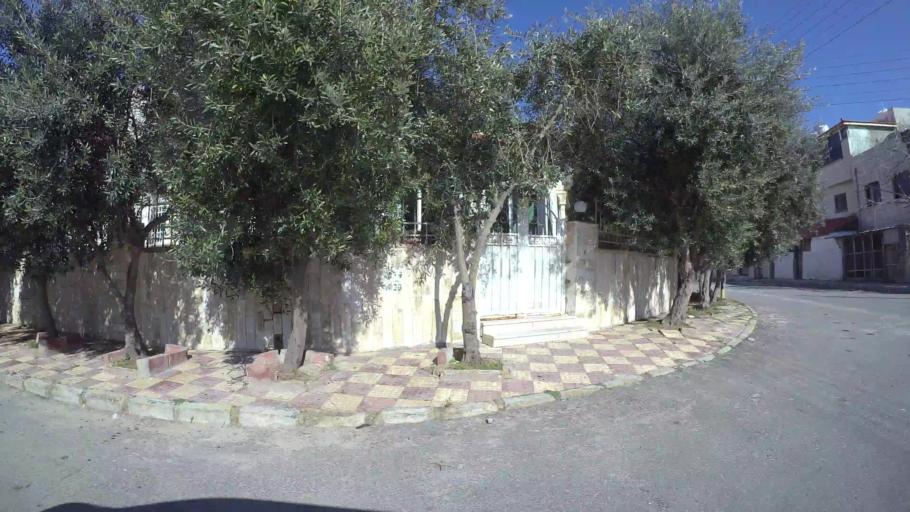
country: JO
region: Amman
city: Al Bunayyat ash Shamaliyah
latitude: 31.9041
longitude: 35.9134
